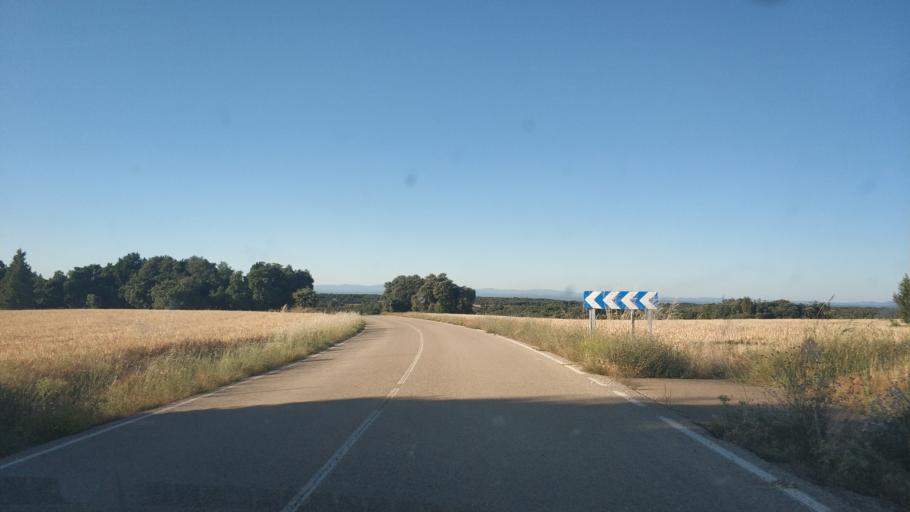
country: ES
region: Castille and Leon
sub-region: Provincia de Soria
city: Liceras
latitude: 41.4534
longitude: -3.2127
